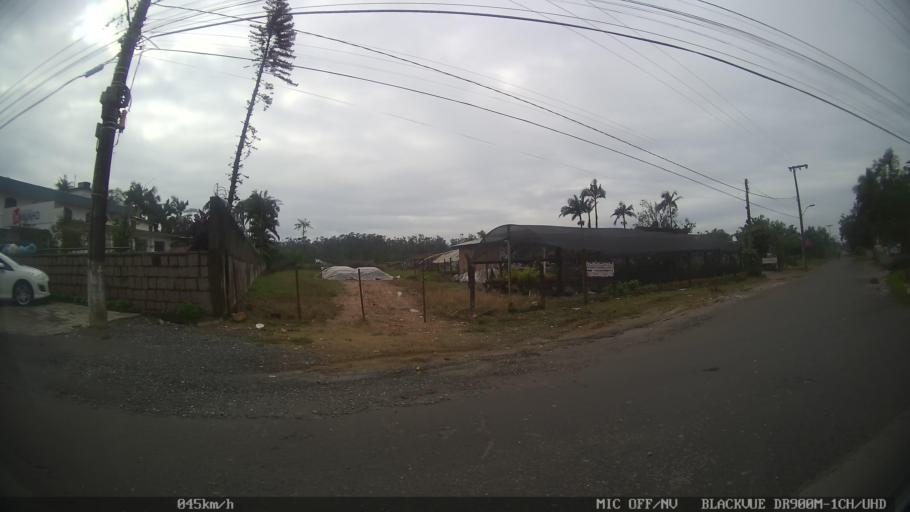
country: BR
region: Santa Catarina
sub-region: Joinville
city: Joinville
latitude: -26.0481
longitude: -48.8566
